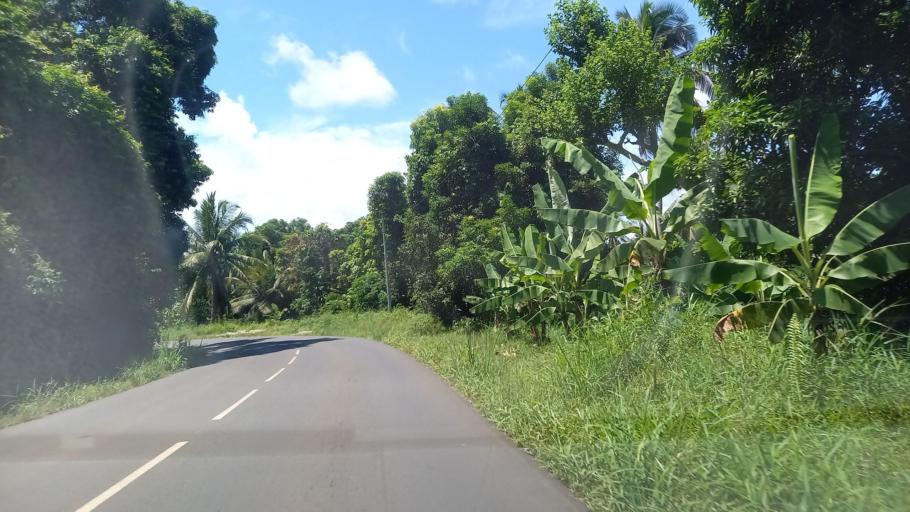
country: YT
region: Sada
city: Sada
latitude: -12.8622
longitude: 45.1113
